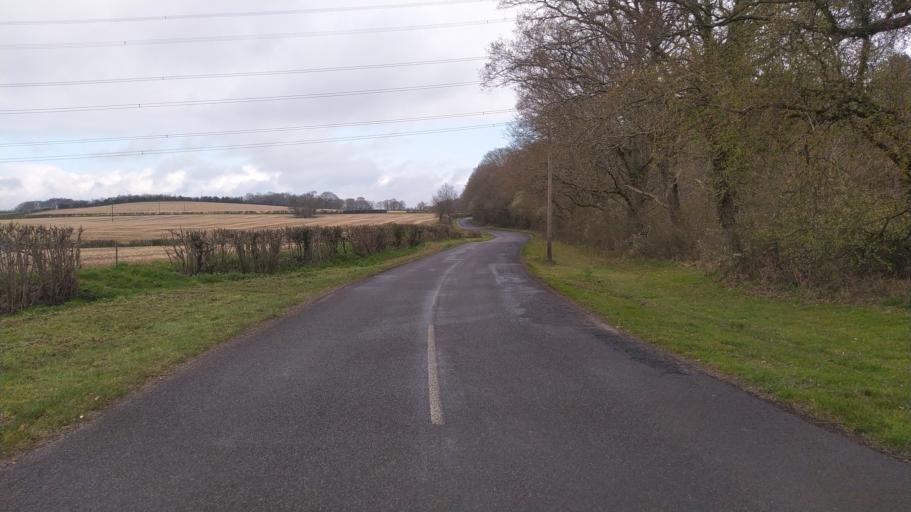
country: GB
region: England
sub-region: West Sussex
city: Petworth
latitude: 51.0150
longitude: -0.6074
